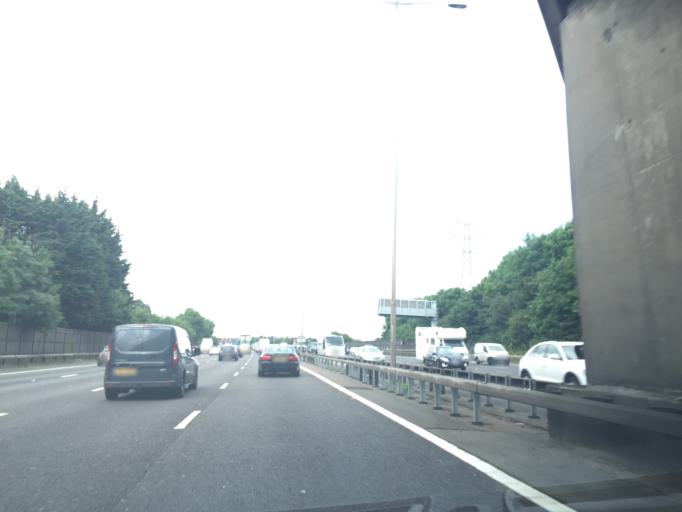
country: GB
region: England
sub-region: Buckinghamshire
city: Iver
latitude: 51.5220
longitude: -0.4985
